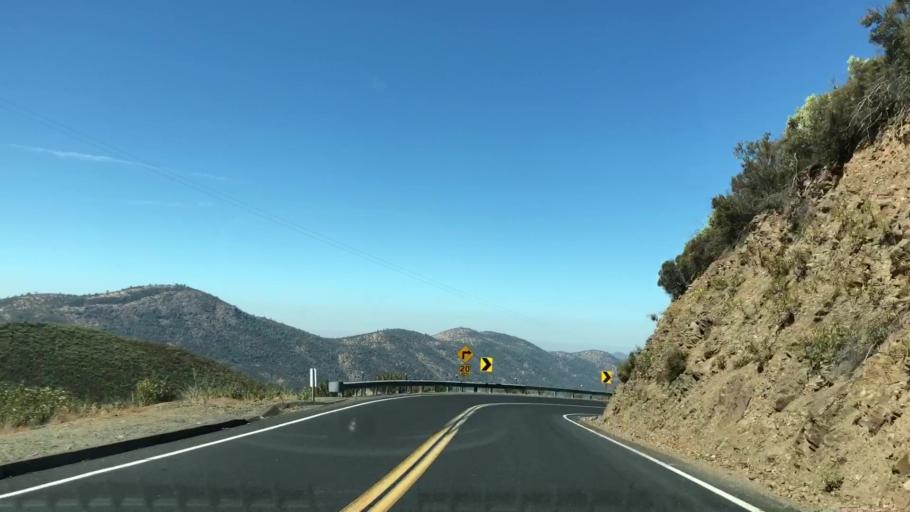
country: US
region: California
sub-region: Tuolumne County
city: Tuolumne City
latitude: 37.8183
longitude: -120.2733
